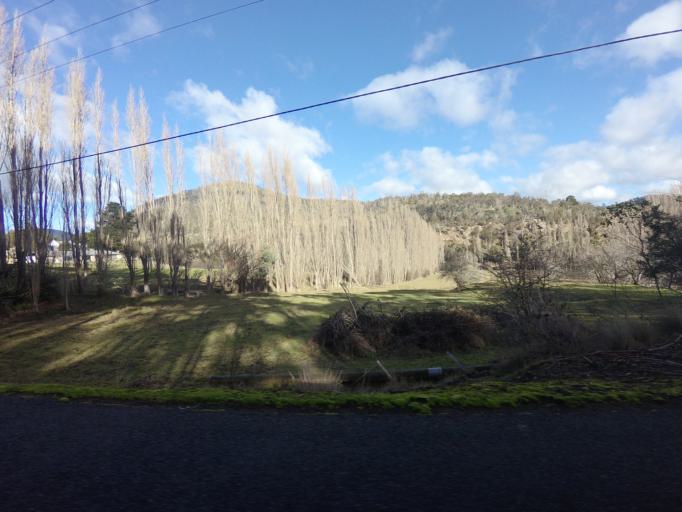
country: AU
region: Tasmania
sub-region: Glenorchy
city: Granton
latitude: -42.8045
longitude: 147.1631
